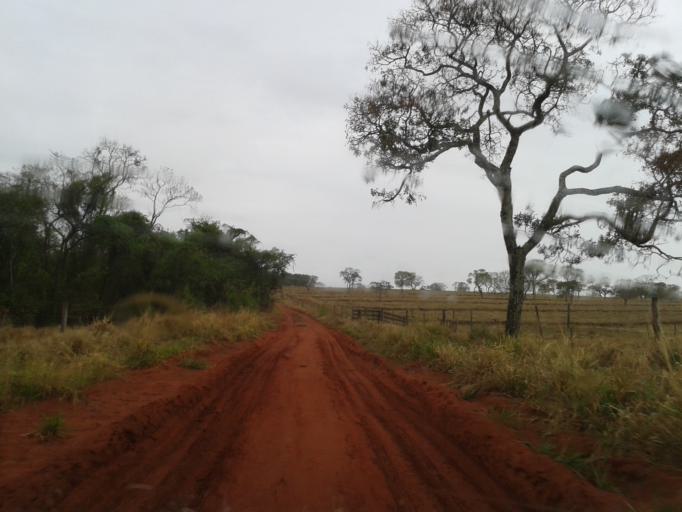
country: BR
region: Minas Gerais
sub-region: Campina Verde
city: Campina Verde
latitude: -19.3544
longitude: -49.5371
